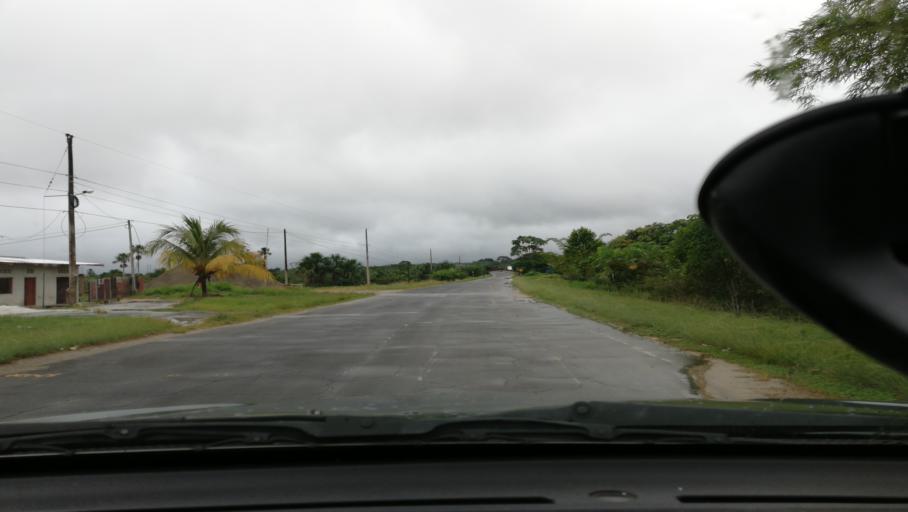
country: PE
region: Loreto
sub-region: Provincia de Loreto
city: Nauta
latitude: -4.2304
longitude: -73.4859
